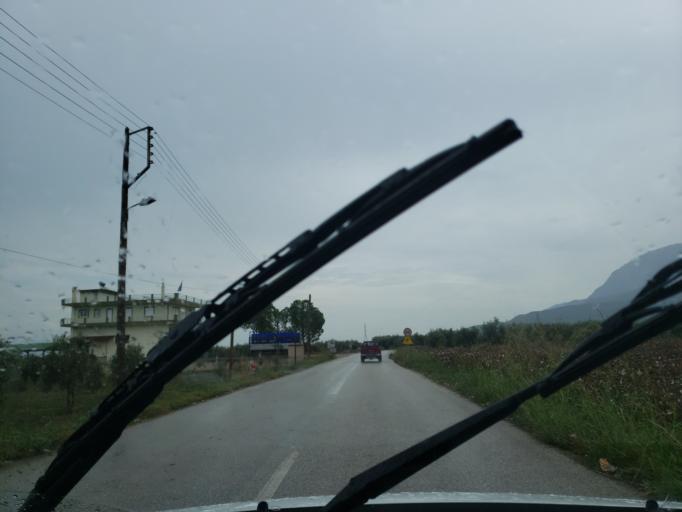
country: GR
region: Central Greece
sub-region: Nomos Fthiotidos
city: Anthili
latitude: 38.8048
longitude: 22.4506
